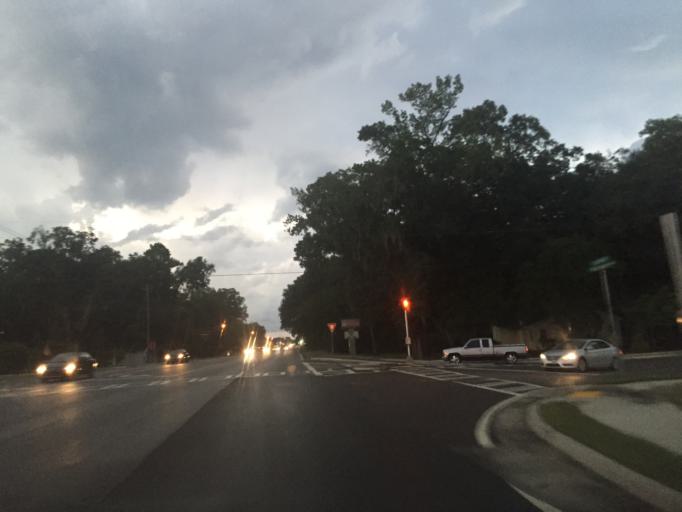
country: US
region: Georgia
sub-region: Liberty County
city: Hinesville
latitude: 31.8486
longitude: -81.5894
